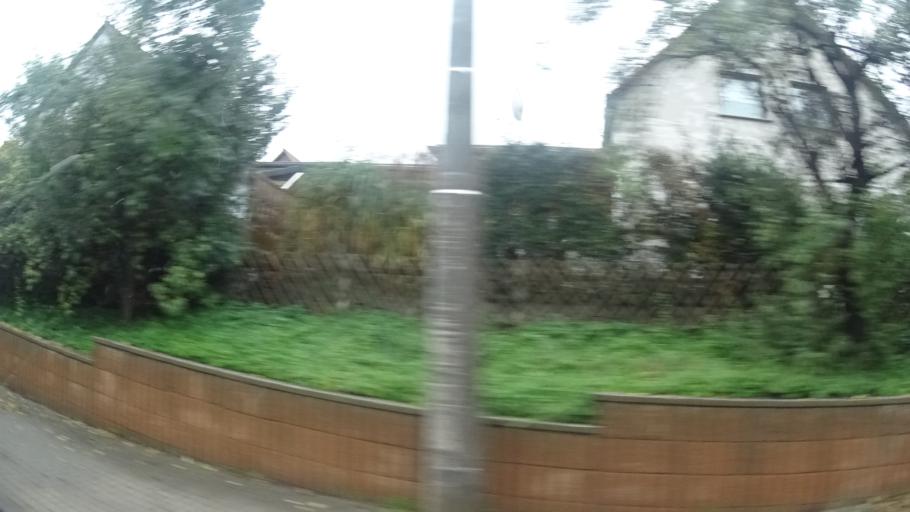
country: DE
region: Thuringia
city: Possneck
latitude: 50.7010
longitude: 11.5830
